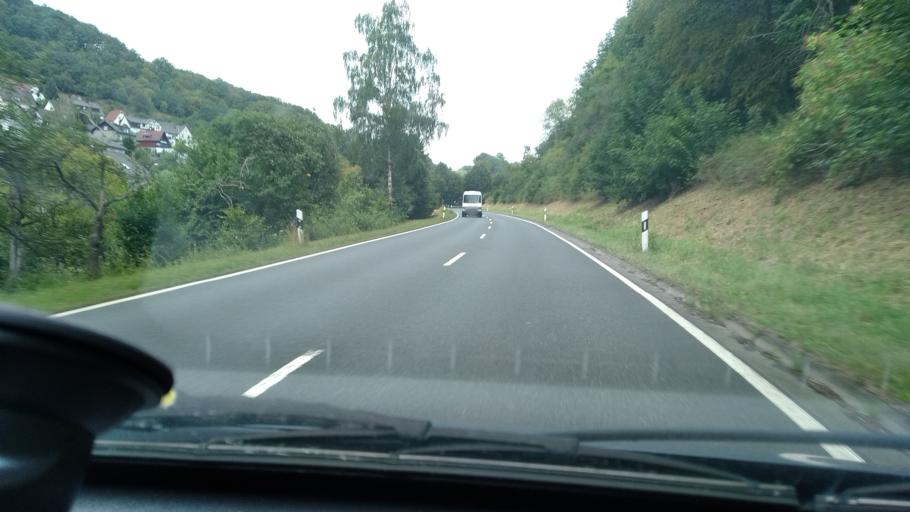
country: DE
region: Hesse
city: Dillenburg
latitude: 50.7701
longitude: 8.3259
